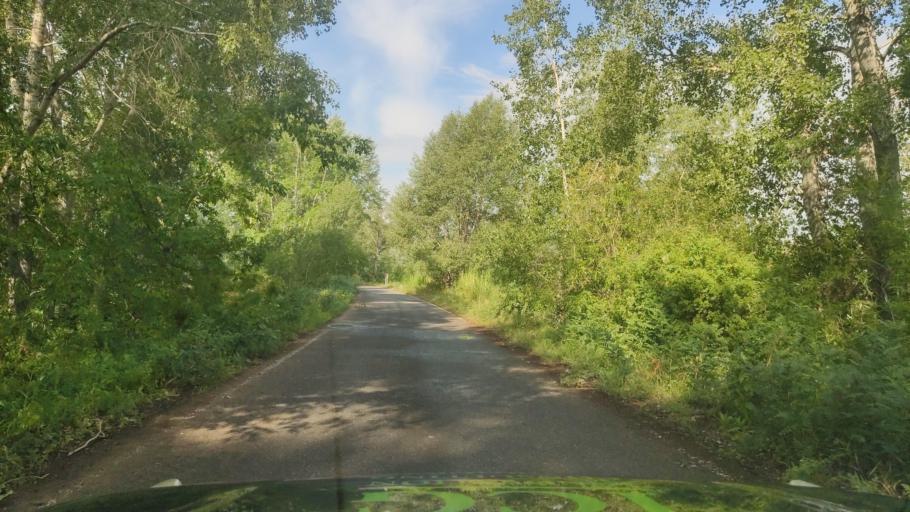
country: KZ
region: Pavlodar
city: Leninskiy
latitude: 52.4770
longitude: 76.8041
